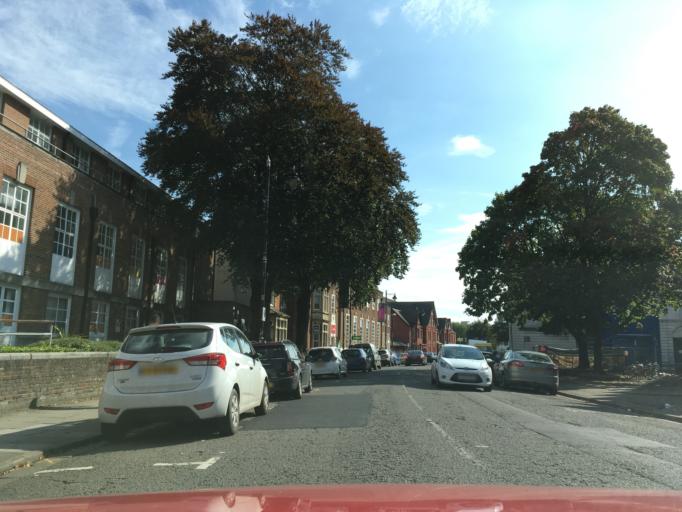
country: GB
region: Wales
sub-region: Cardiff
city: Cardiff
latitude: 51.4889
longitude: -3.1800
